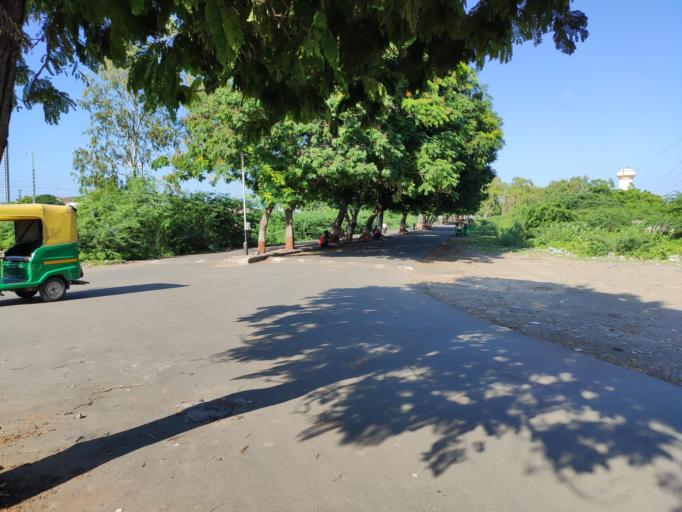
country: IN
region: Gujarat
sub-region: Jamnagar
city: Bedi
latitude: 22.4905
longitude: 70.0503
